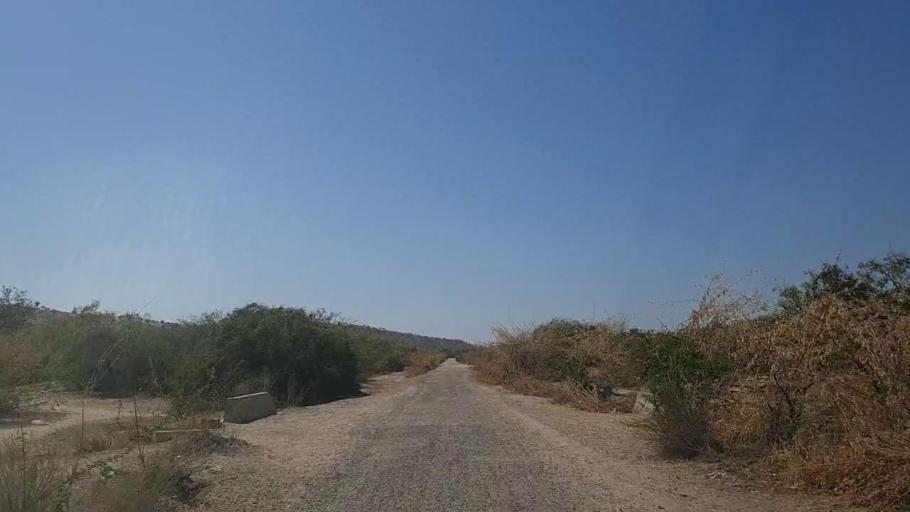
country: PK
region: Sindh
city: Mithi
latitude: 24.7982
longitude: 69.7141
